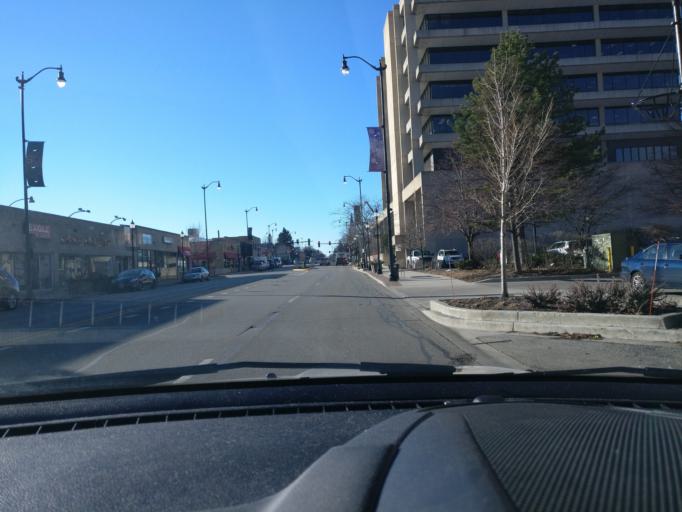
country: US
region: Illinois
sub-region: Cook County
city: Skokie
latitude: 42.0263
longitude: -87.7527
